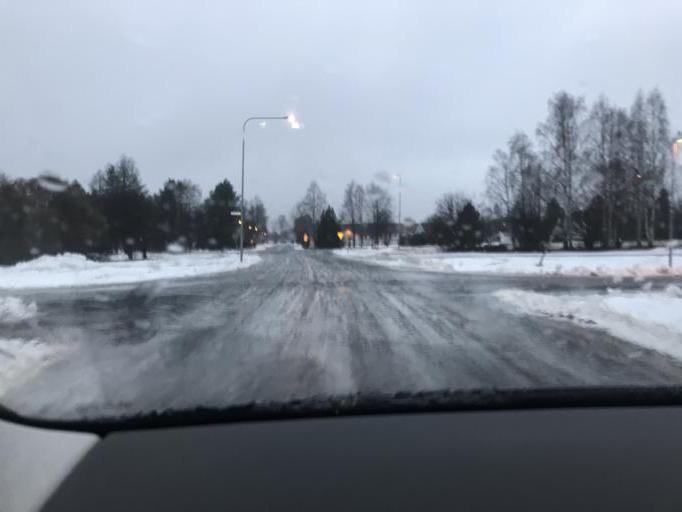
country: SE
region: Norrbotten
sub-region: Lulea Kommun
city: Sodra Sunderbyn
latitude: 65.6505
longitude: 21.9623
